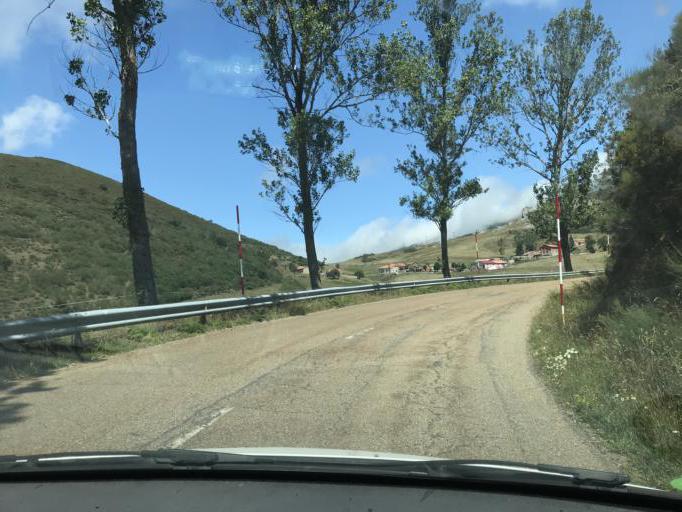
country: ES
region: Castille and Leon
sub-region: Provincia de Palencia
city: Polentinos
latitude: 43.0332
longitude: -4.4610
